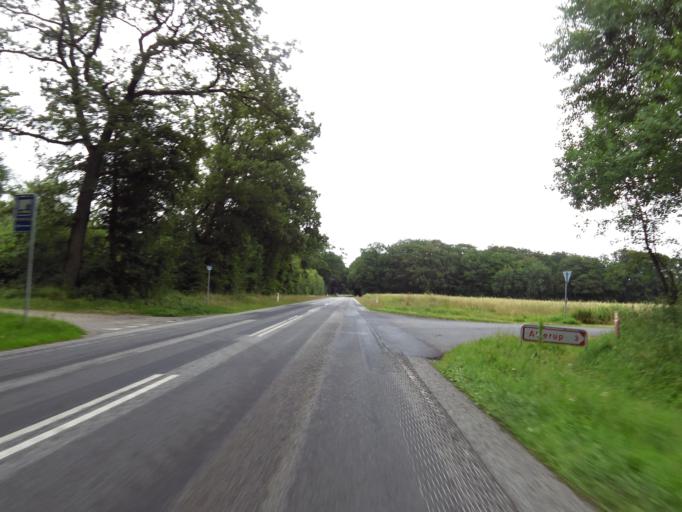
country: DK
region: South Denmark
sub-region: Tonder Kommune
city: Toftlund
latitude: 55.1916
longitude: 8.9635
